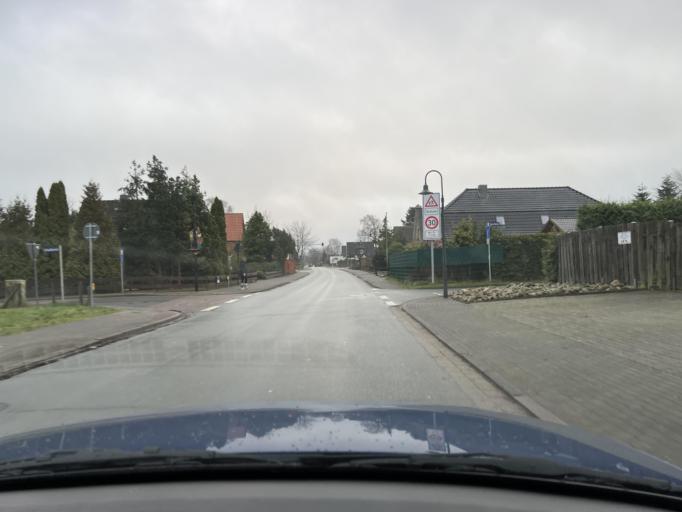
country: DE
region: Schleswig-Holstein
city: Lohe-Rickelshof
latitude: 54.2107
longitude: 9.0739
